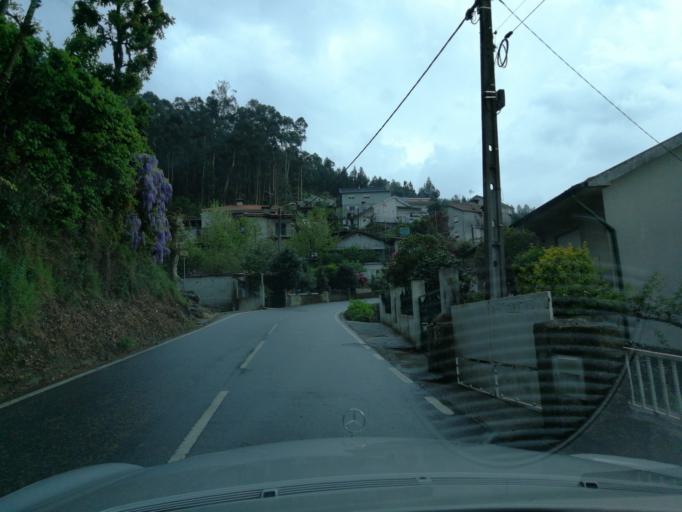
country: PT
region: Braga
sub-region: Braga
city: Oliveira
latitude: 41.4662
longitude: -8.4742
